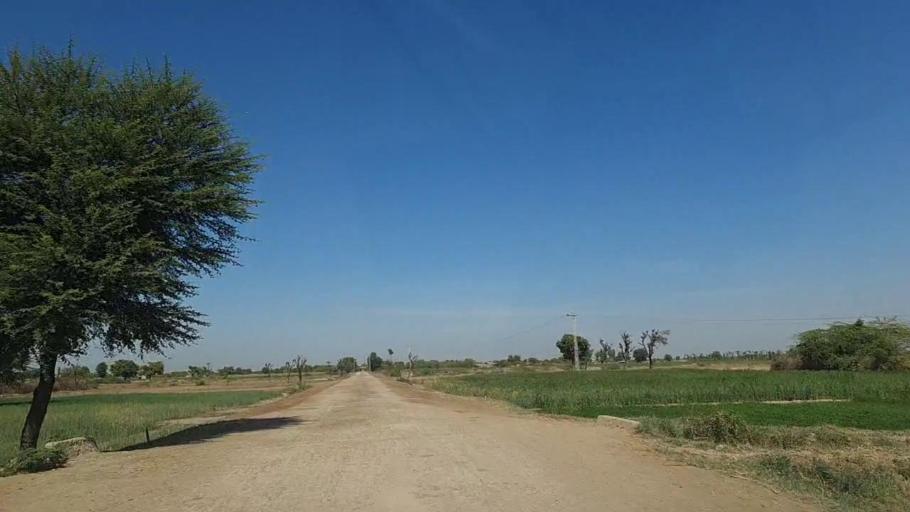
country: PK
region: Sindh
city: Samaro
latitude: 25.3025
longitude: 69.5019
